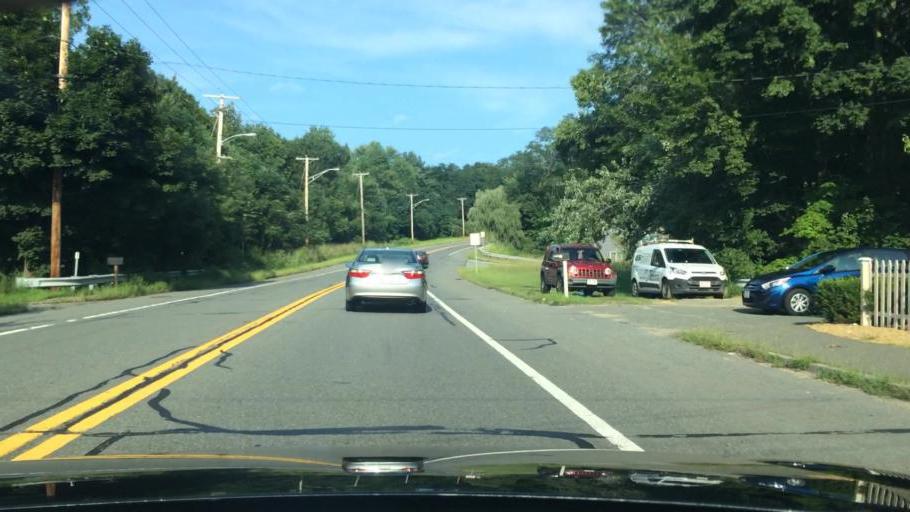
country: US
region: Massachusetts
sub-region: Essex County
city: Haverhill
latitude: 42.7751
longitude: -71.1282
